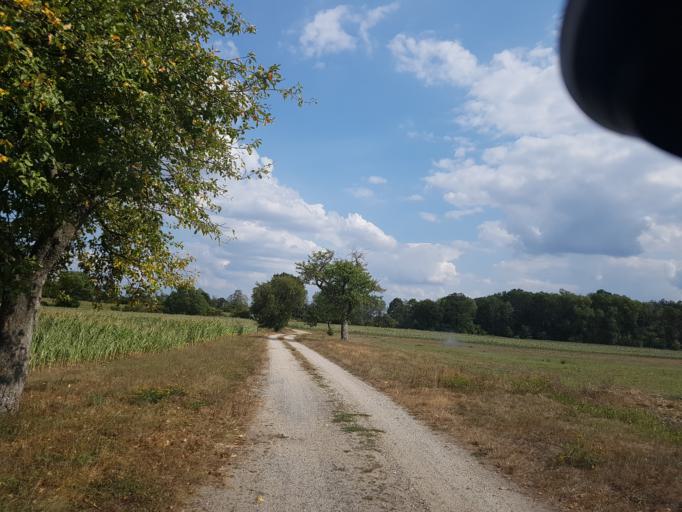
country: DE
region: Brandenburg
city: Calau
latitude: 51.7728
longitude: 13.9613
